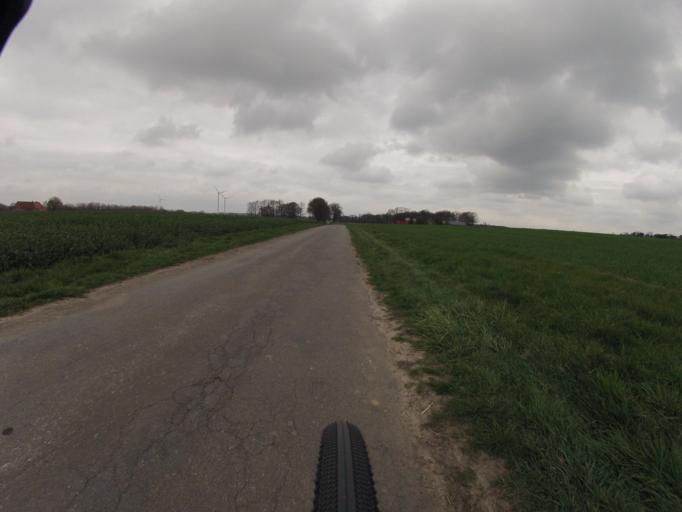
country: DE
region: North Rhine-Westphalia
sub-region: Regierungsbezirk Munster
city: Mettingen
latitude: 52.3313
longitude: 7.8213
